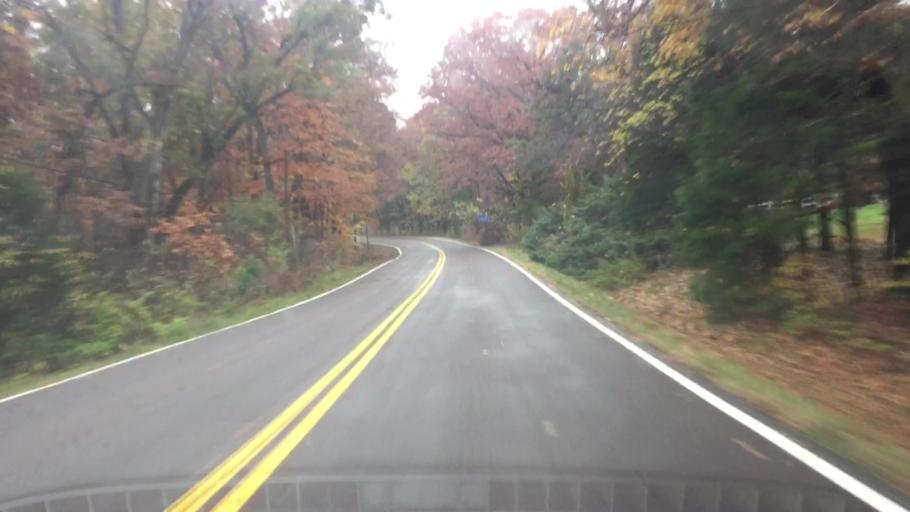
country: US
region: Missouri
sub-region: Boone County
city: Columbia
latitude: 38.8681
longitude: -92.3180
